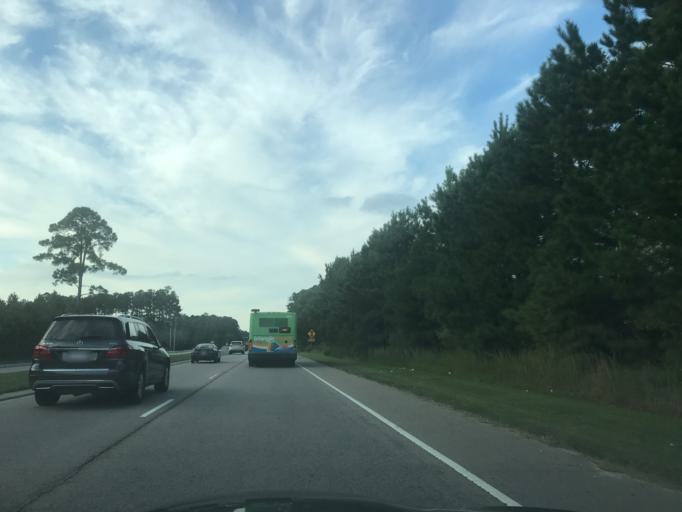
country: US
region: North Carolina
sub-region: Wake County
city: Green Level
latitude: 35.8092
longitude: -78.8720
